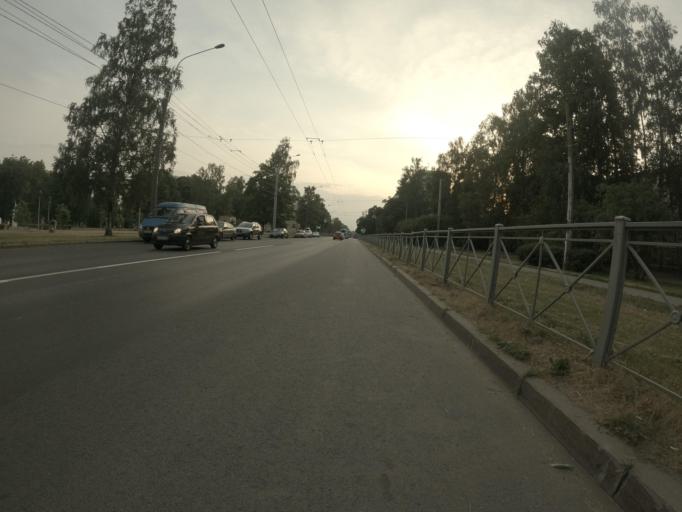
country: RU
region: Leningrad
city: Kalininskiy
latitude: 59.9842
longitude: 30.4192
